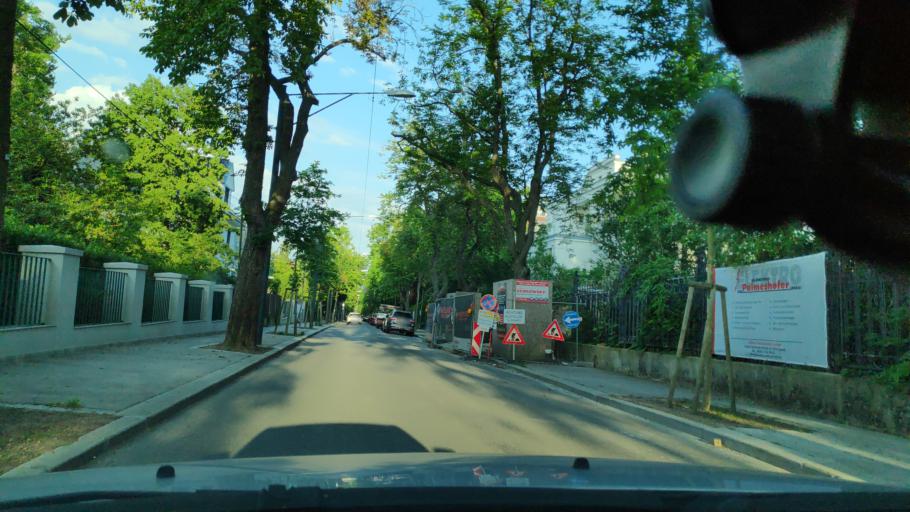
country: AT
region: Vienna
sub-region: Wien Stadt
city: Vienna
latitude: 48.2267
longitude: 16.3004
